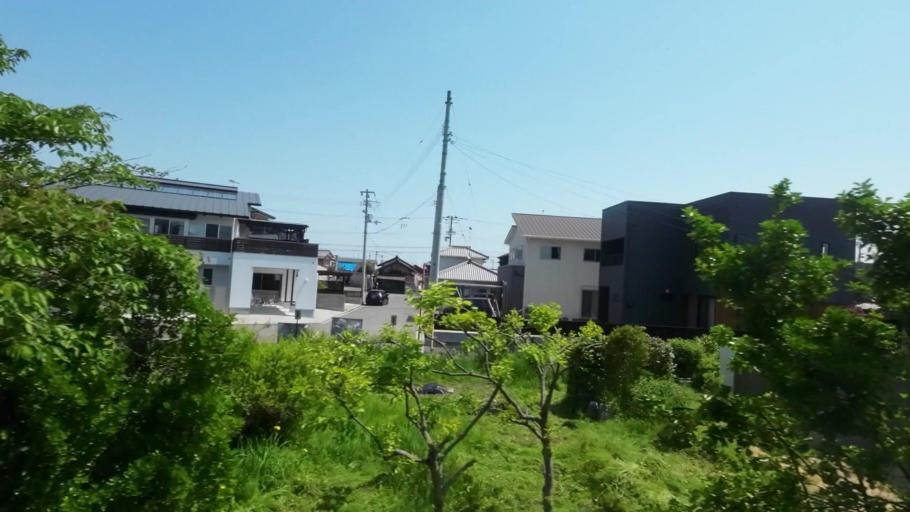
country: JP
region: Ehime
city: Saijo
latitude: 33.9310
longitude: 133.0845
